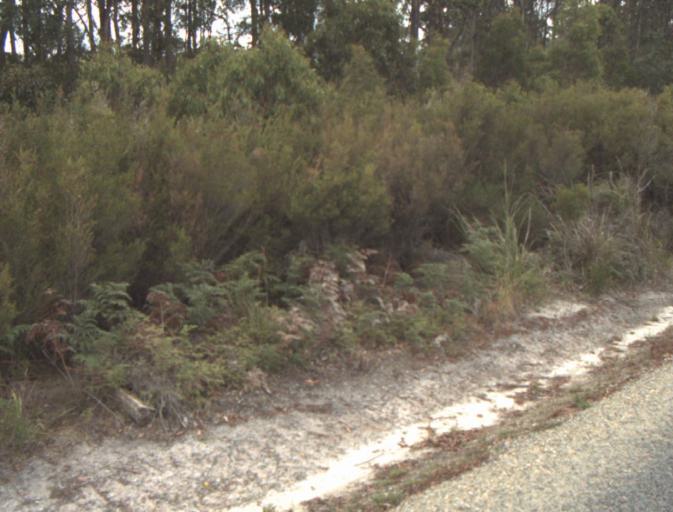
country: AU
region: Tasmania
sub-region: Launceston
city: Mayfield
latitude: -41.2108
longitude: 147.1887
